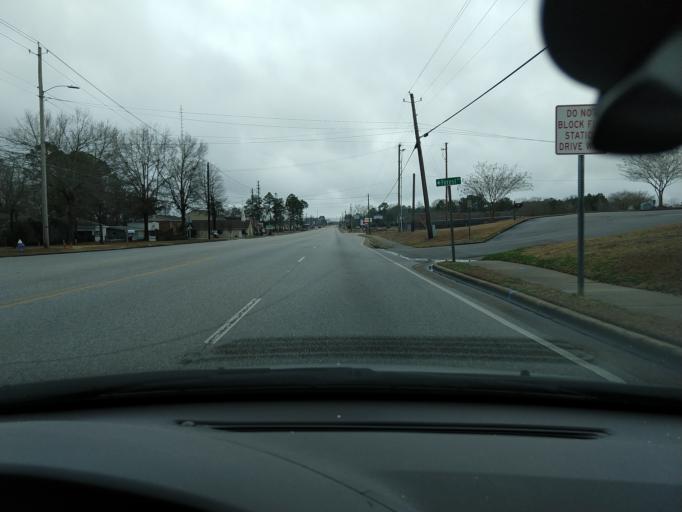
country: US
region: Alabama
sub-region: Houston County
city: Dothan
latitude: 31.2355
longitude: -85.4346
